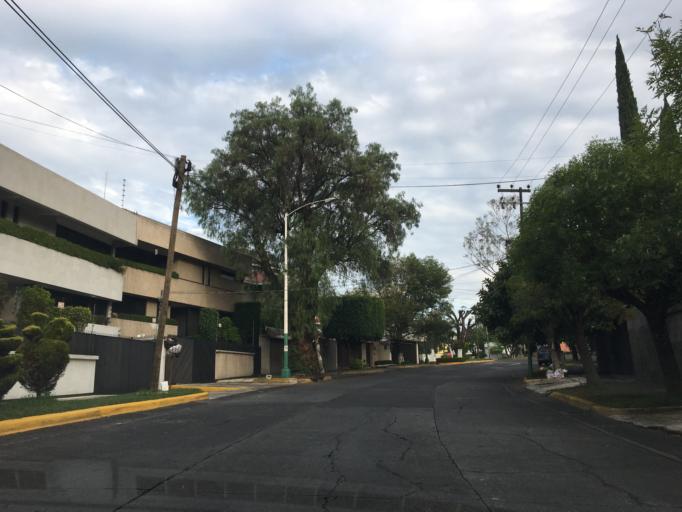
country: MX
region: Mexico
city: Naucalpan de Juarez
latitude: 19.4985
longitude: -99.2481
